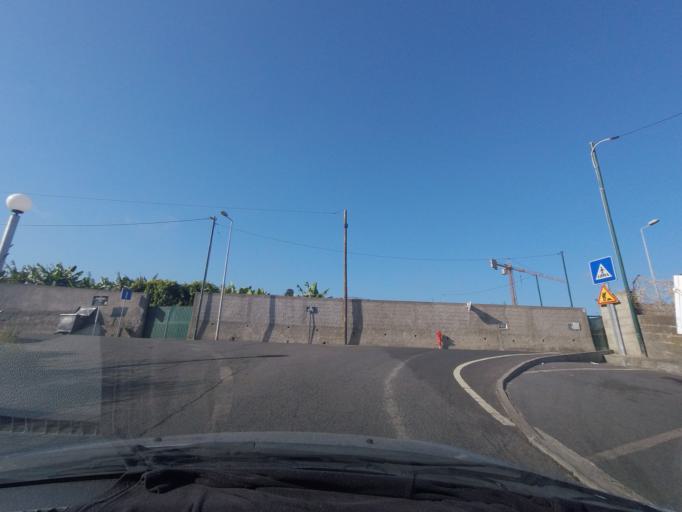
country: PT
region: Madeira
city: Camara de Lobos
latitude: 32.6535
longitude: -16.9440
